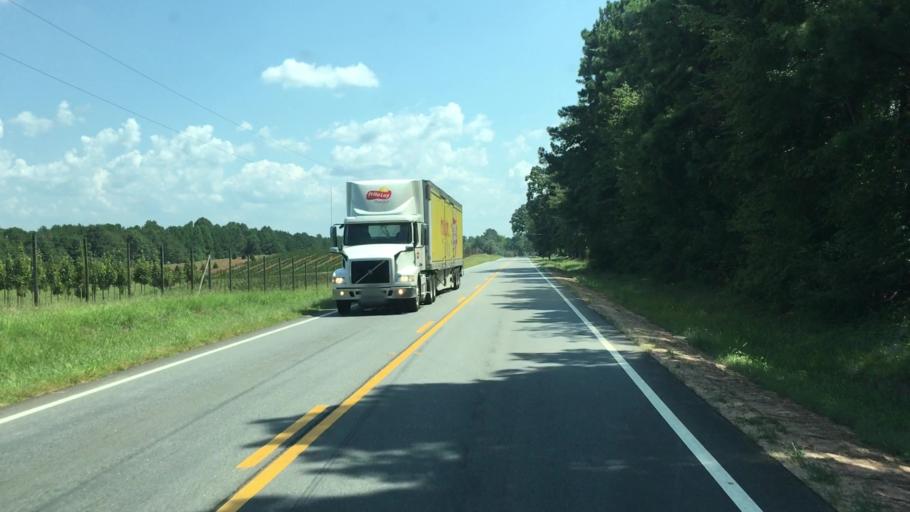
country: US
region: Georgia
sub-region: Oconee County
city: Watkinsville
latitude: 33.7482
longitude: -83.4337
